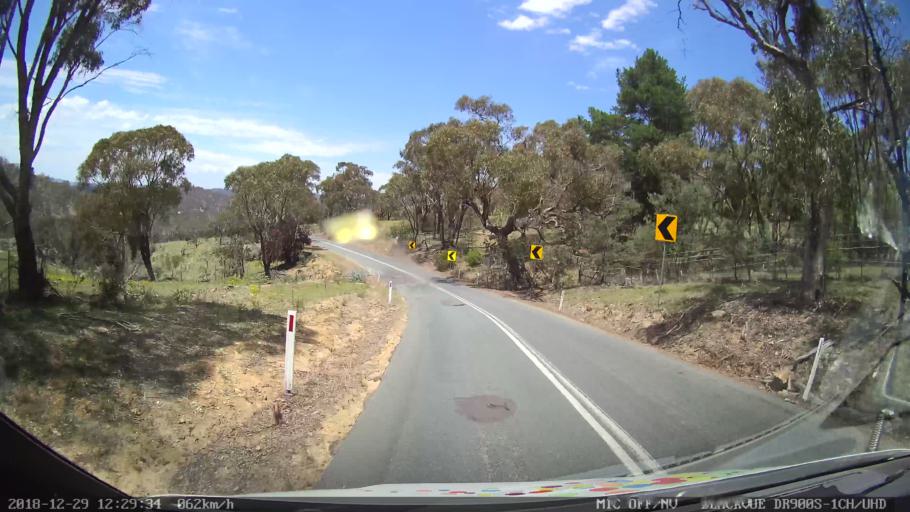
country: AU
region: Australian Capital Territory
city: Macarthur
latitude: -35.4992
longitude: 149.2306
